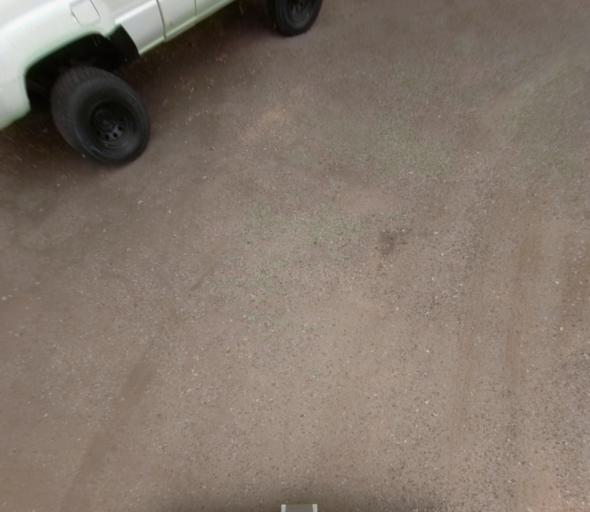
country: US
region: California
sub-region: Madera County
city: Oakhurst
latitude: 37.3430
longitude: -119.6306
